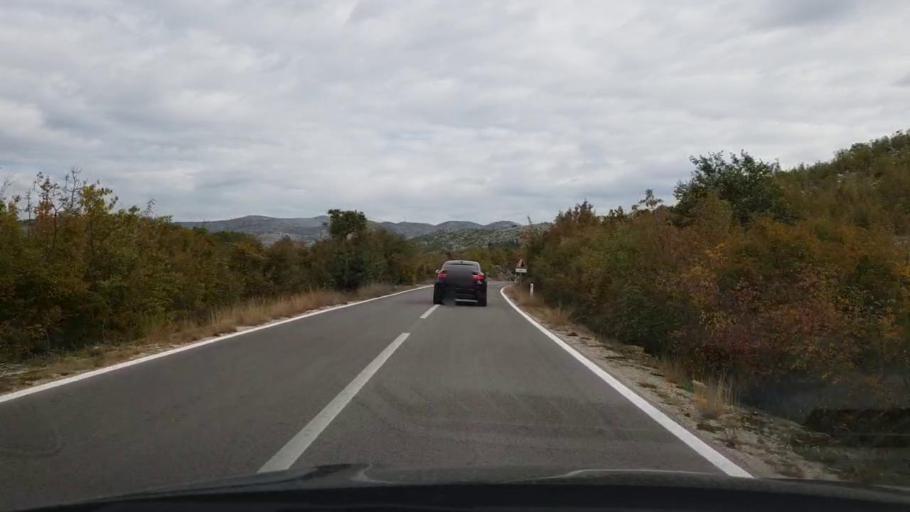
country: BA
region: Republika Srpska
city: Trebinje
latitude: 42.6833
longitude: 18.2939
